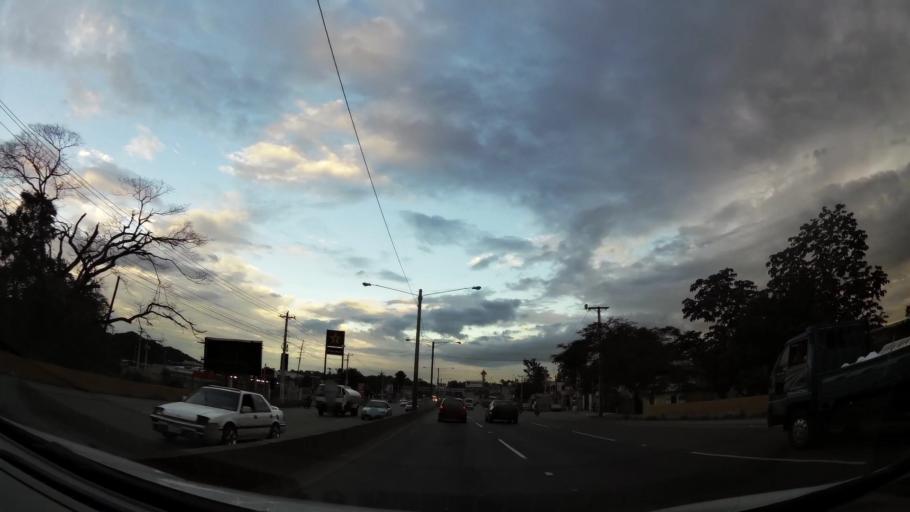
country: DO
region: Santo Domingo
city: Santo Domingo Oeste
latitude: 18.5394
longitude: -70.0290
